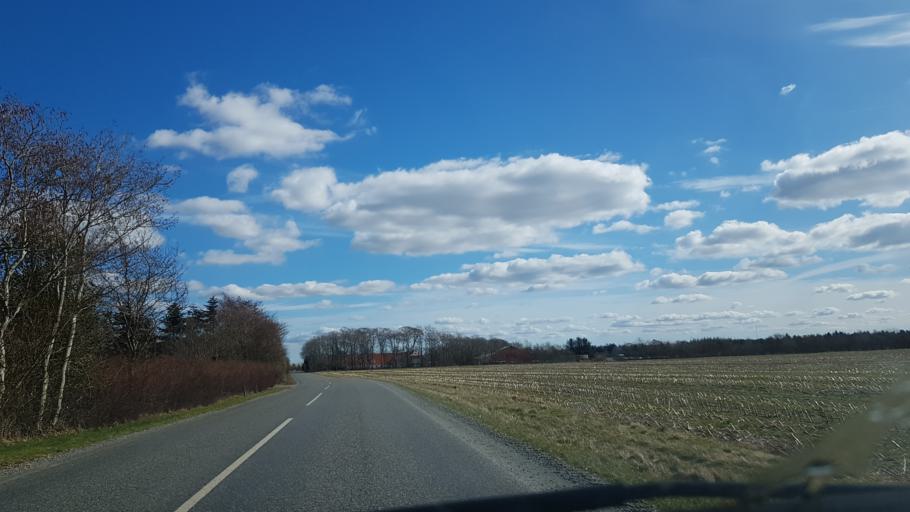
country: DK
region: South Denmark
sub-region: Esbjerg Kommune
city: Ribe
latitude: 55.4014
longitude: 8.8265
